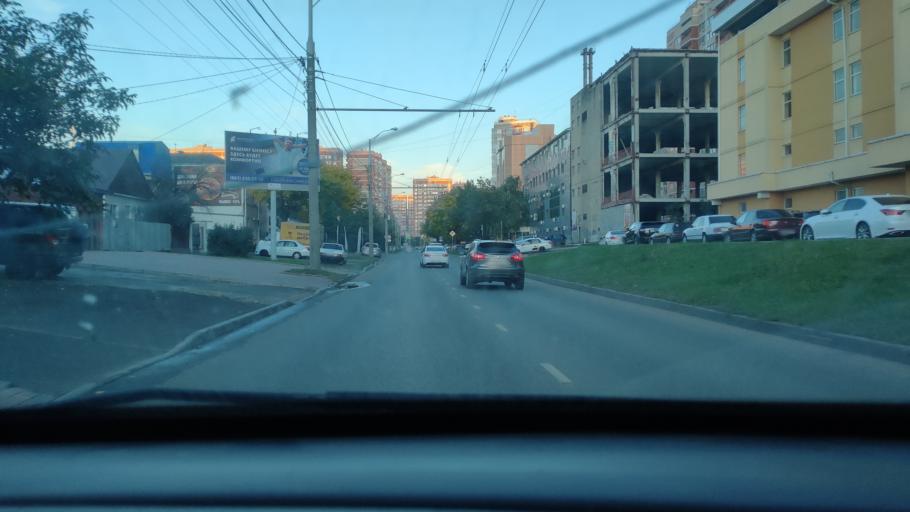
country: RU
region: Krasnodarskiy
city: Krasnodar
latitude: 45.0385
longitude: 38.9443
